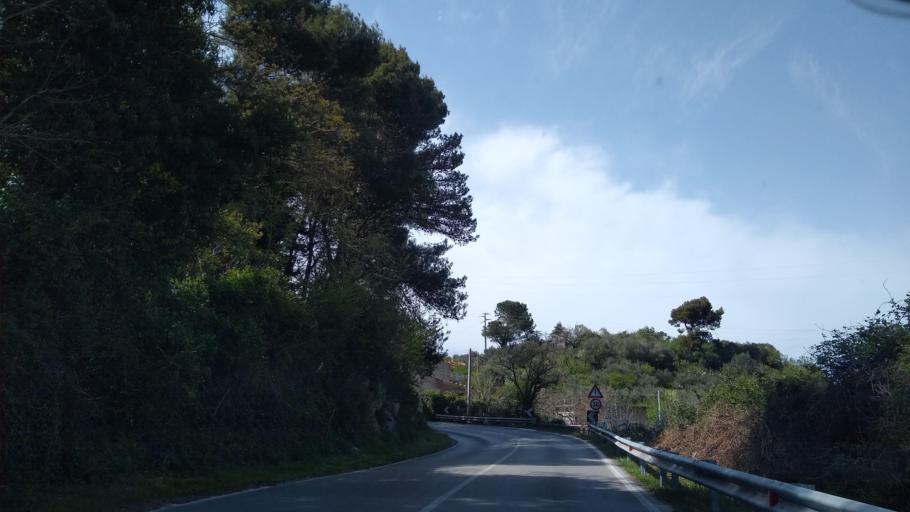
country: IT
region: Sicily
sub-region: Palermo
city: Pioppo
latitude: 38.0409
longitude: 13.2025
